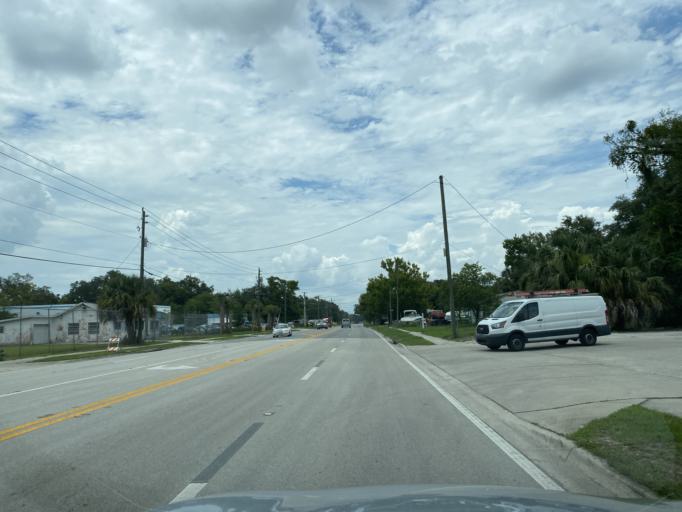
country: US
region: Florida
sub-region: Seminole County
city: Sanford
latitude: 28.7797
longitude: -81.2647
